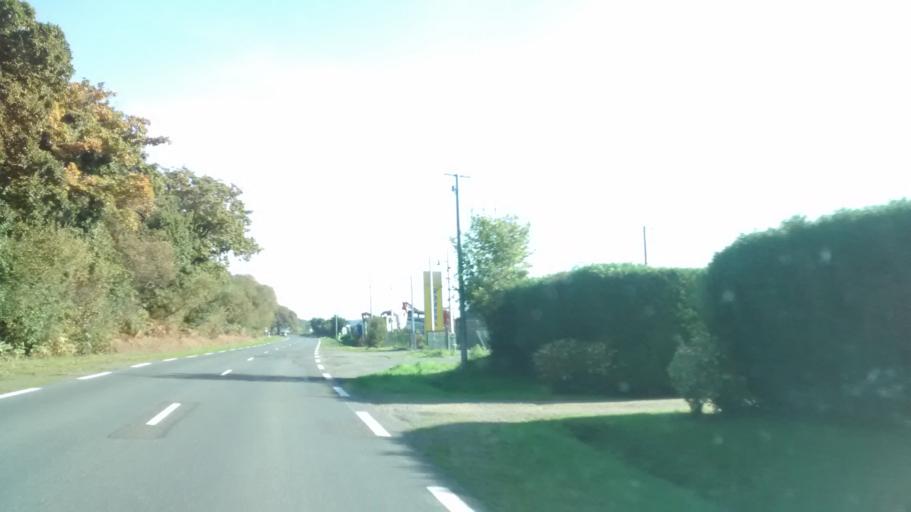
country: FR
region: Brittany
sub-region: Departement des Cotes-d'Armor
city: Pleumeur-Bodou
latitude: 48.7529
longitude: -3.5127
